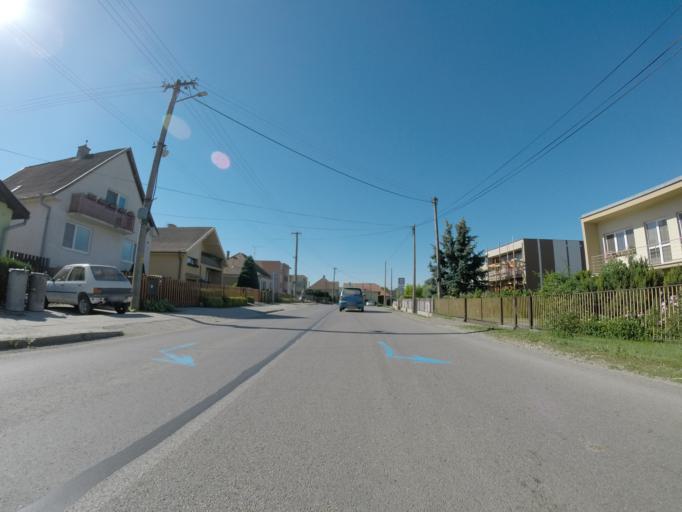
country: SK
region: Trnavsky
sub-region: Okres Trnava
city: Piestany
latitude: 48.5061
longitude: 17.9860
